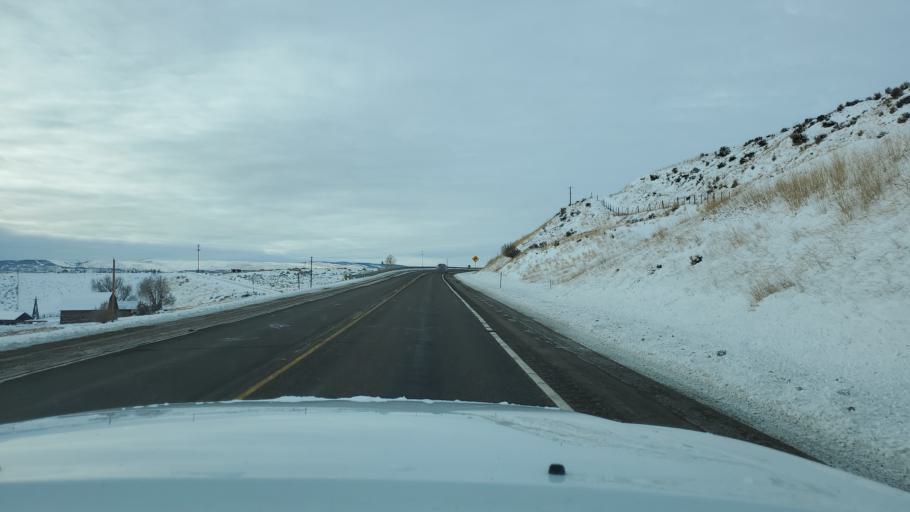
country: US
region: Colorado
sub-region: Moffat County
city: Craig
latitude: 40.5157
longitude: -107.4877
